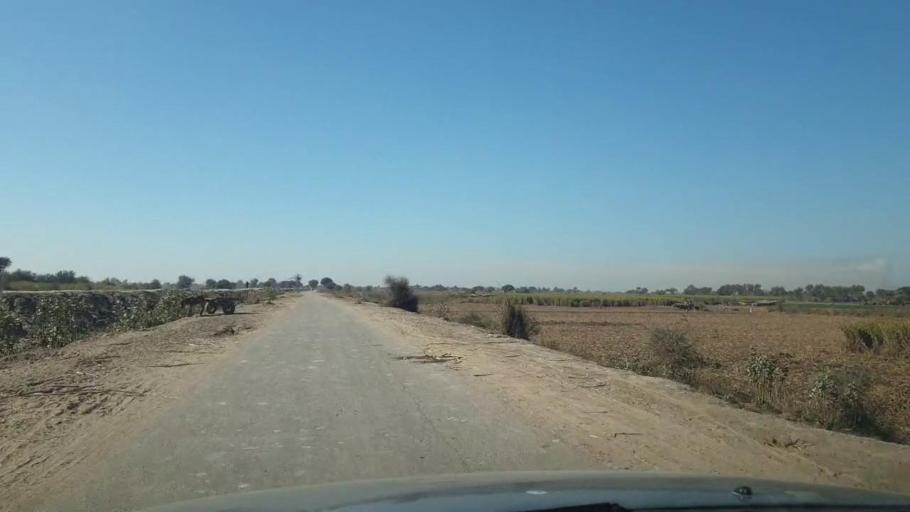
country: PK
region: Sindh
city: Ghotki
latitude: 28.0311
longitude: 69.2802
